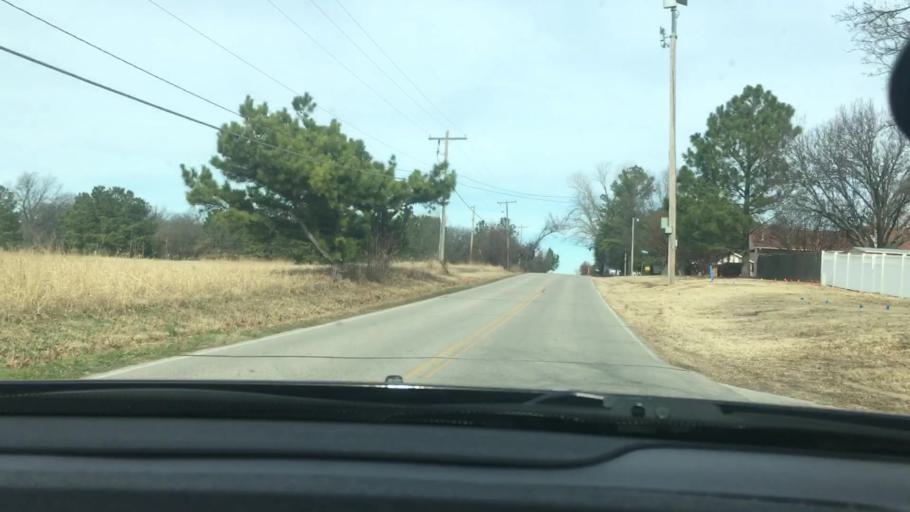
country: US
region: Oklahoma
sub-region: Carter County
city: Ardmore
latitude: 34.1743
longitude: -97.0731
